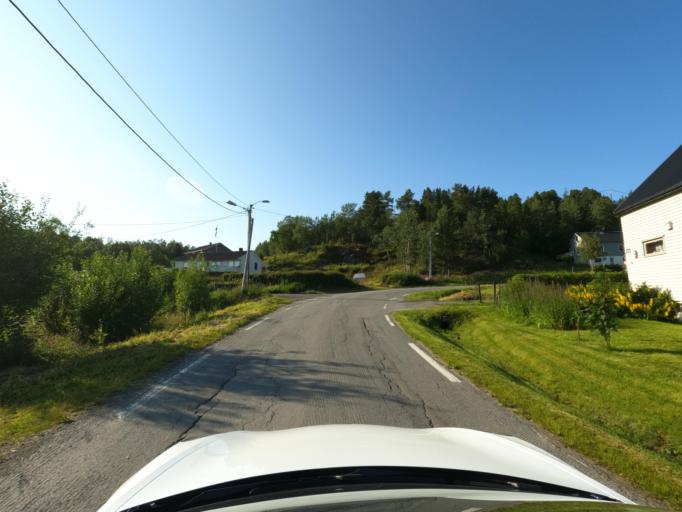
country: NO
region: Nordland
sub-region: Narvik
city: Narvik
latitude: 68.4711
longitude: 17.5036
